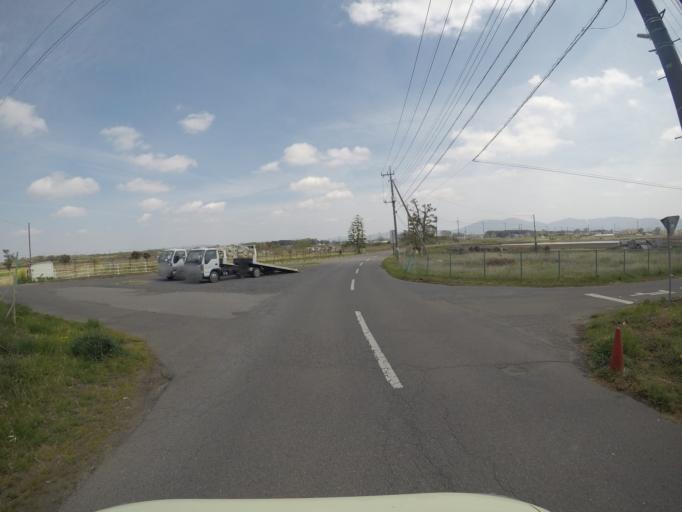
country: JP
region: Ibaraki
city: Shimodate
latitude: 36.2724
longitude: 140.0180
